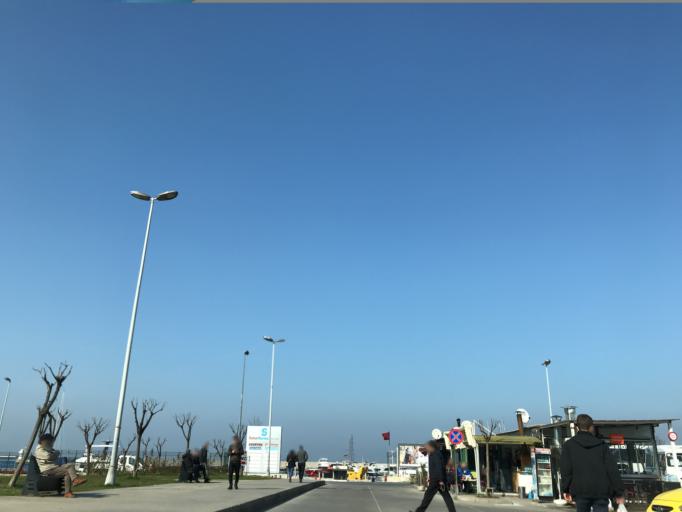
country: TR
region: Yalova
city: Yalova
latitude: 40.6593
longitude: 29.2765
